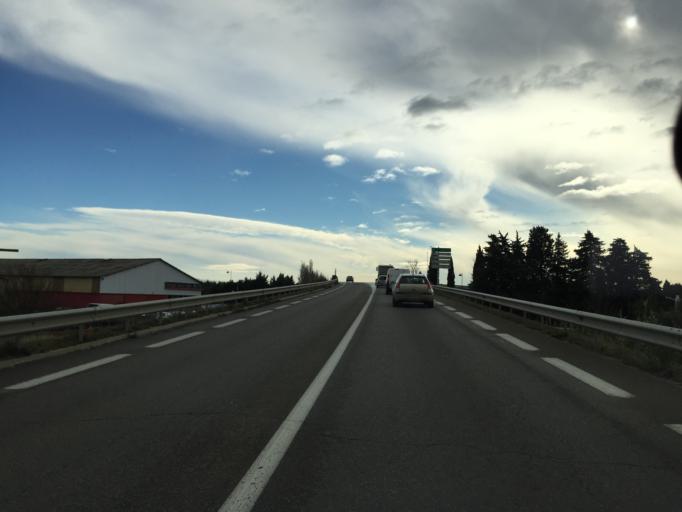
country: FR
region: Provence-Alpes-Cote d'Azur
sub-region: Departement du Vaucluse
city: L'Isle-sur-la-Sorgue
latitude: 43.9205
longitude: 5.0289
